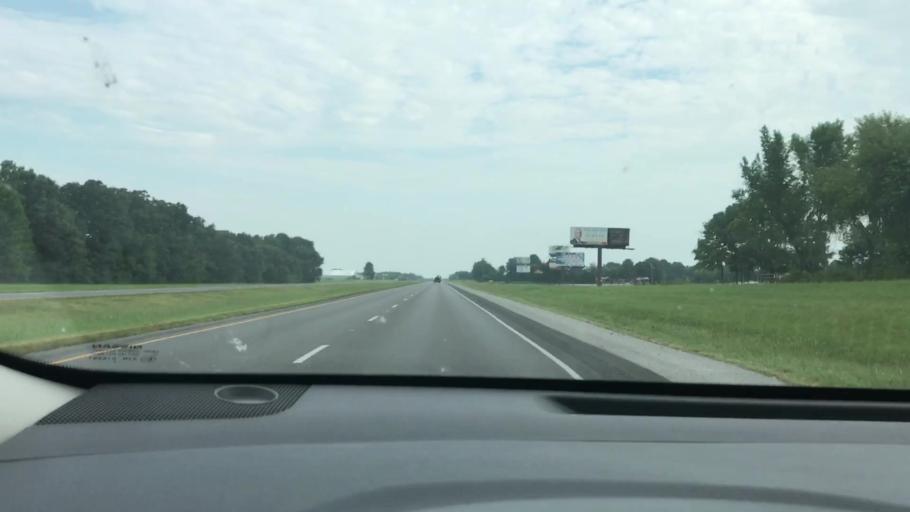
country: US
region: Kentucky
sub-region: Calloway County
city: Murray
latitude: 36.6837
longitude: -88.3027
